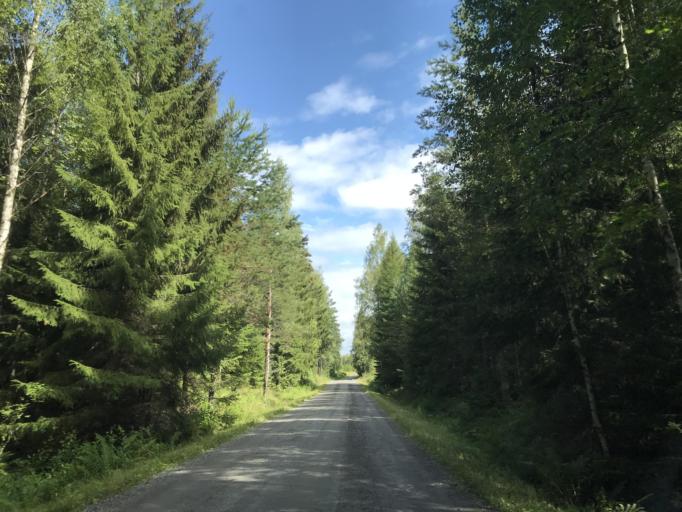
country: FI
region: Uusimaa
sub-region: Helsinki
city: Kaerkoelae
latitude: 60.6365
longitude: 23.8092
